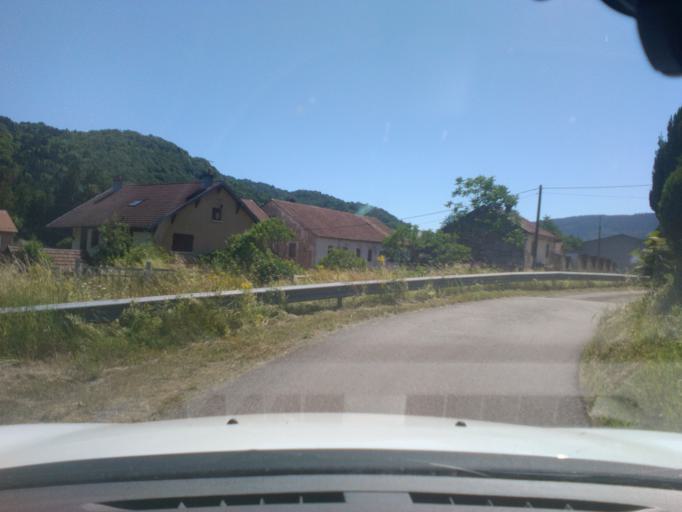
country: FR
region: Lorraine
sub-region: Departement des Vosges
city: Saulxures-sur-Moselotte
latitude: 47.9543
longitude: 6.7418
